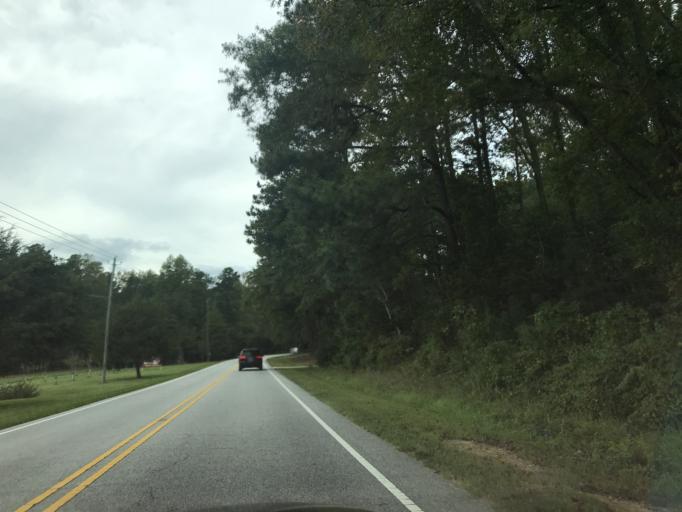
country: US
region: North Carolina
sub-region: Franklin County
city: Youngsville
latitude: 36.0040
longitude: -78.4319
